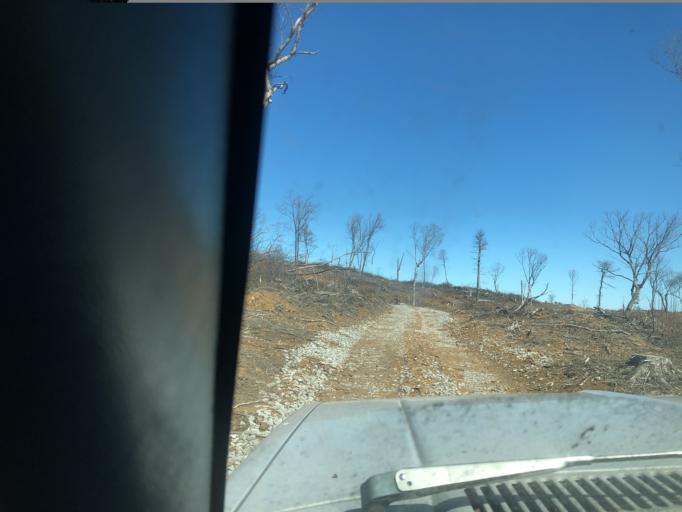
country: US
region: Tennessee
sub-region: Cumberland County
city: Fairfield Glade
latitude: 35.9724
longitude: -84.7663
